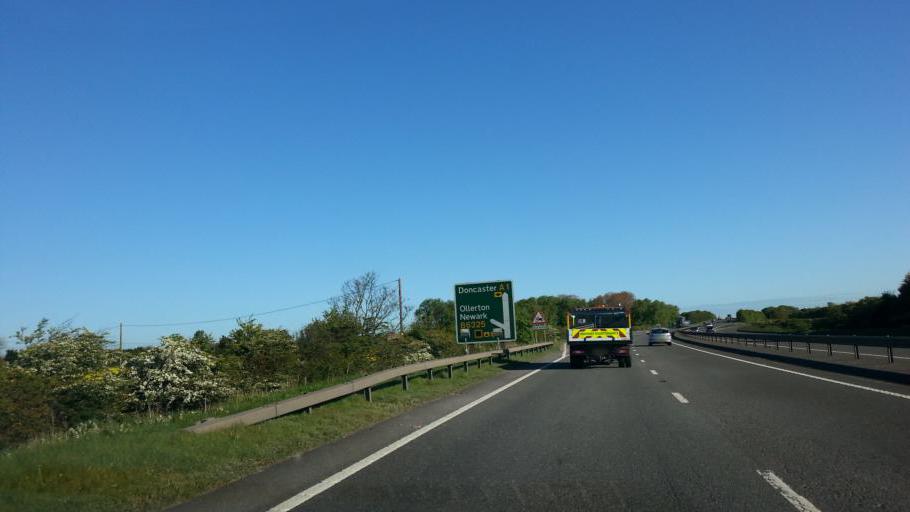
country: GB
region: England
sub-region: Nottinghamshire
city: Newark on Trent
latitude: 53.1143
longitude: -0.8158
